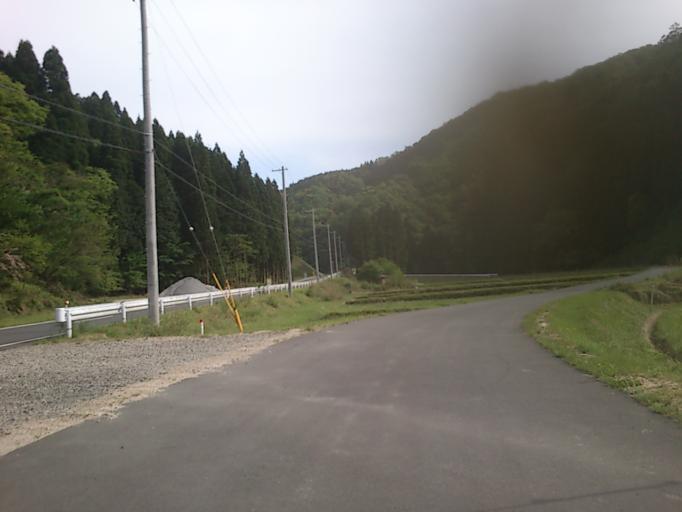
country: JP
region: Kyoto
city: Miyazu
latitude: 35.6369
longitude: 135.0132
